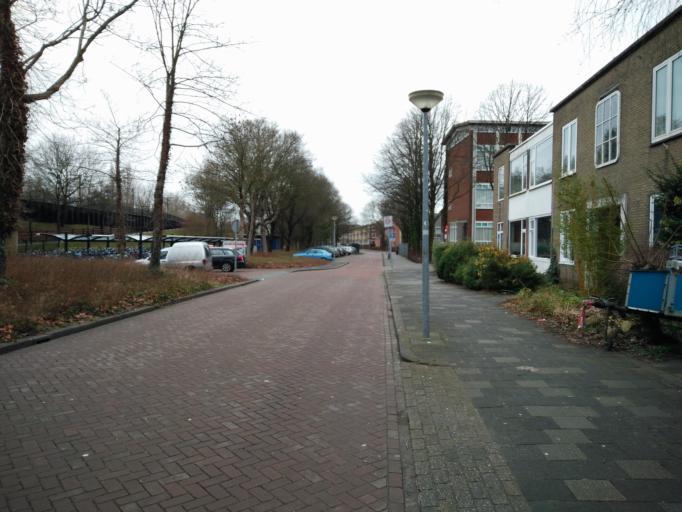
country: NL
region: Groningen
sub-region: Gemeente Groningen
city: Korrewegwijk
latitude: 53.2300
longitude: 6.5572
